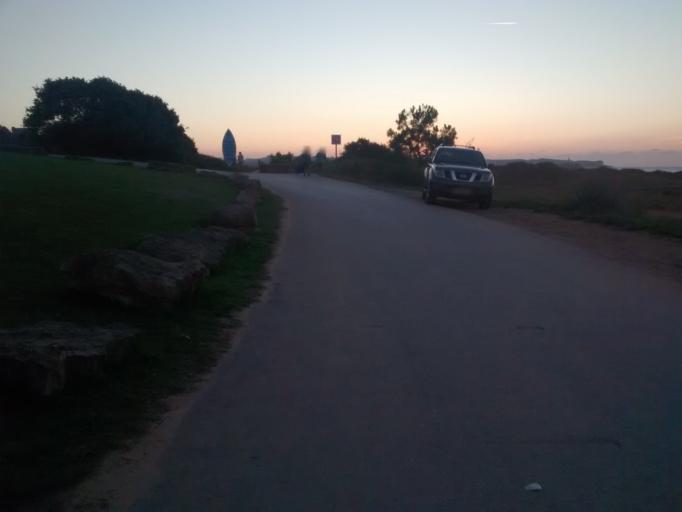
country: ES
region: Cantabria
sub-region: Provincia de Cantabria
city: Santander
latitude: 43.4591
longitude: -3.7271
